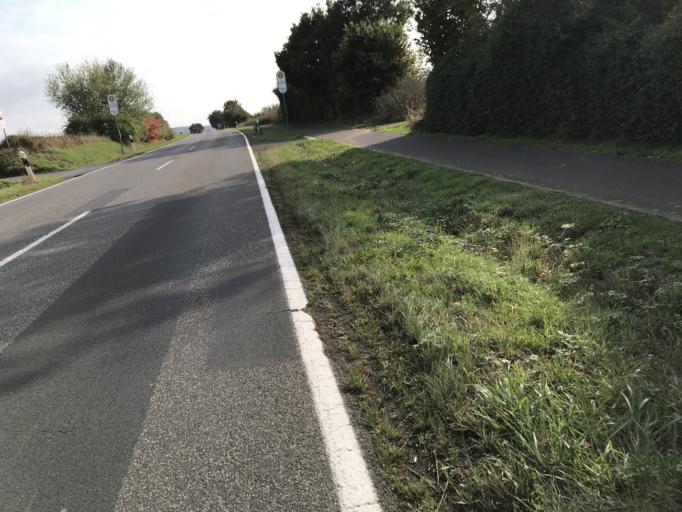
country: DE
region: Hesse
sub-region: Regierungsbezirk Giessen
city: Langgons
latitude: 50.5119
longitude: 8.6540
